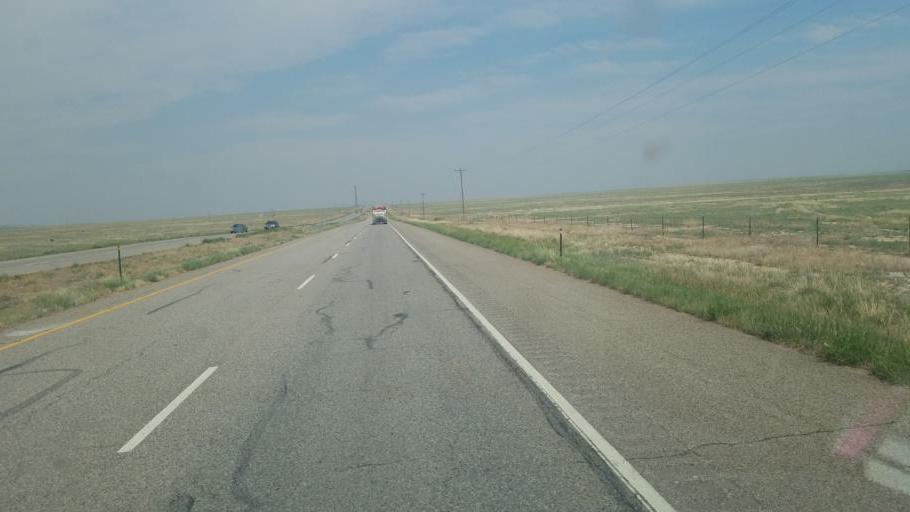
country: US
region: Colorado
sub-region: Fremont County
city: Penrose
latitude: 38.3640
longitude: -104.8940
